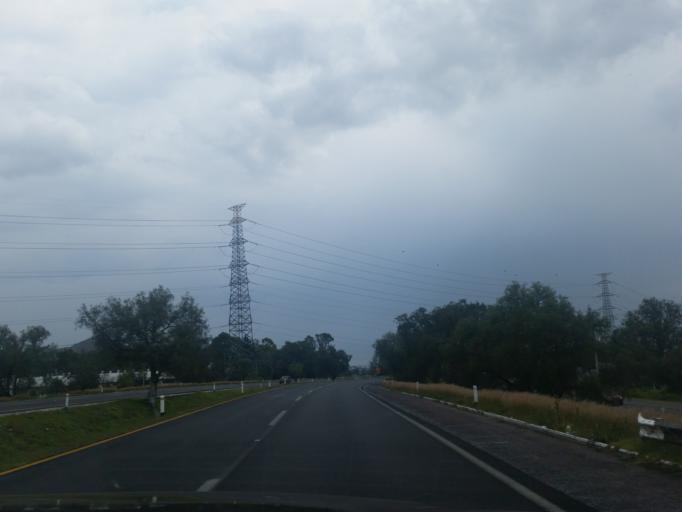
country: MX
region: Morelos
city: Xometla
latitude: 19.6621
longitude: -98.8720
